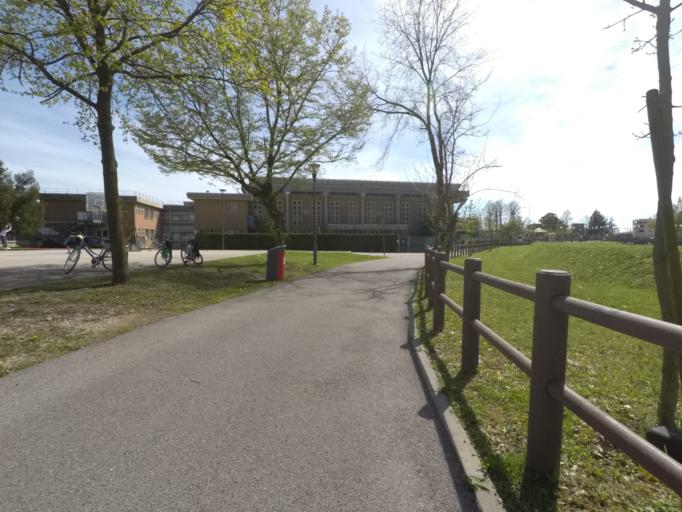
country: IT
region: Friuli Venezia Giulia
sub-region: Provincia di Pordenone
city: Fiume Veneto
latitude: 45.9300
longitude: 12.7320
